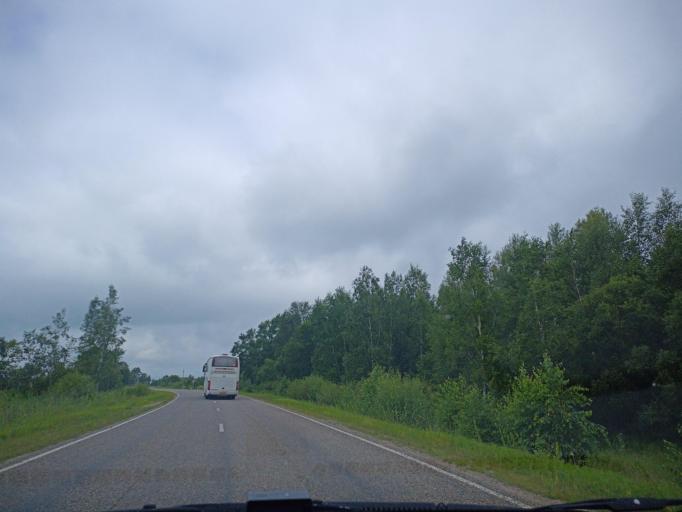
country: RU
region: Primorskiy
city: Novopokrovka
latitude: 45.9743
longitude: 134.2147
